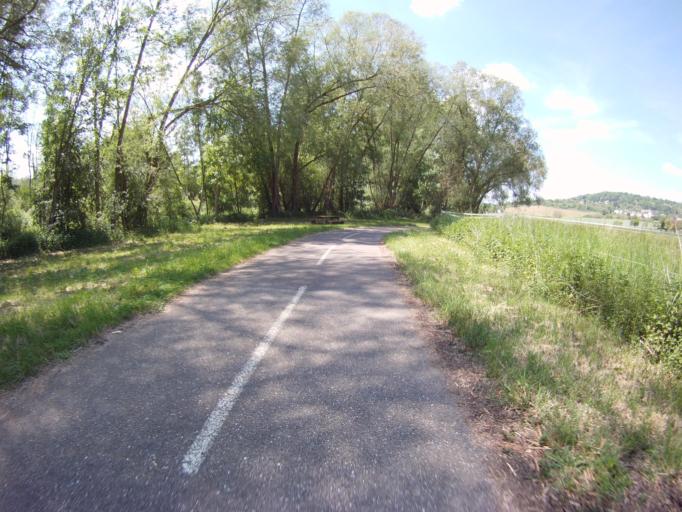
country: FR
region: Lorraine
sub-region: Departement de Meurthe-et-Moselle
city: Eulmont
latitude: 48.7410
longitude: 6.2246
